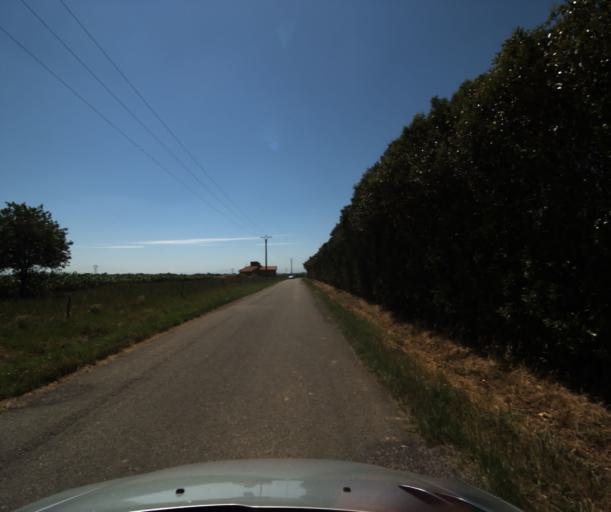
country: FR
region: Midi-Pyrenees
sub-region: Departement de la Haute-Garonne
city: Roquettes
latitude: 43.4890
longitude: 1.3680
